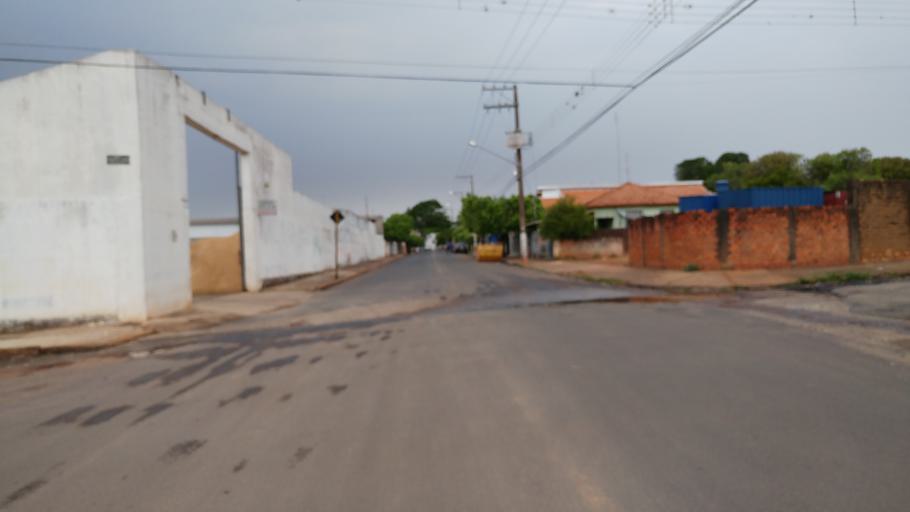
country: BR
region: Sao Paulo
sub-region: Paraguacu Paulista
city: Paraguacu Paulista
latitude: -22.4240
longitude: -50.5770
